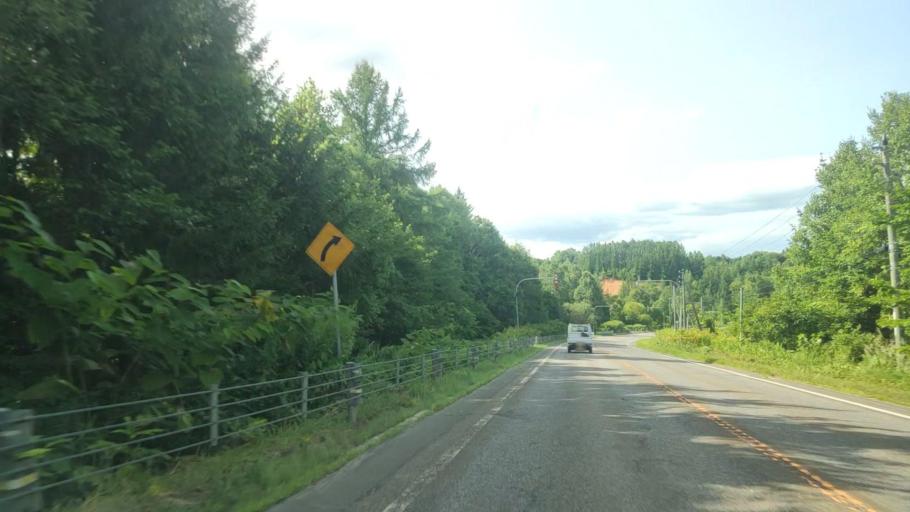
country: JP
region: Hokkaido
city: Nayoro
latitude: 44.3924
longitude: 142.3953
